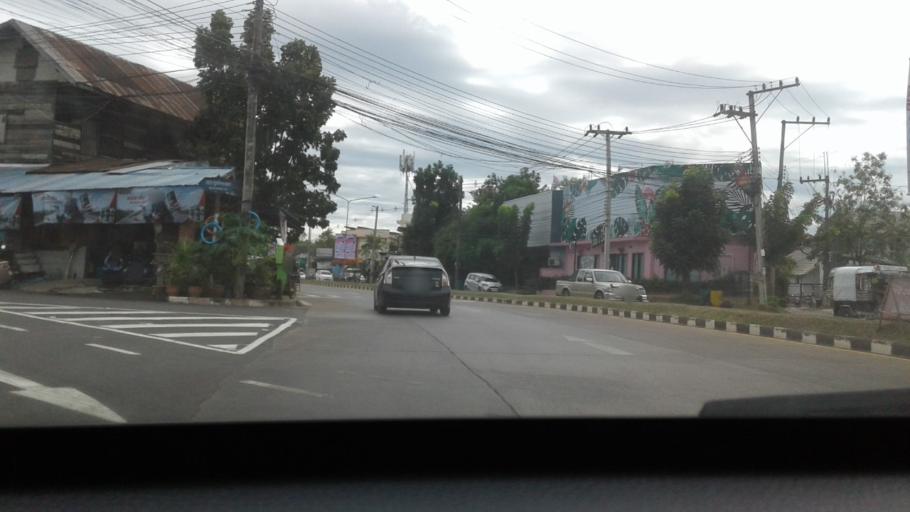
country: TH
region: Changwat Udon Thani
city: Udon Thani
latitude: 17.4209
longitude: 102.7843
